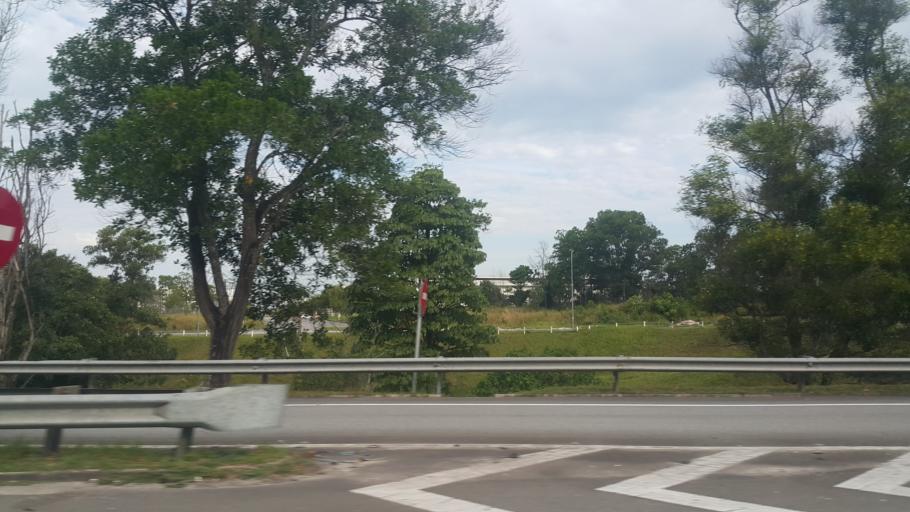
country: MY
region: Johor
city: Skudai
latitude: 1.4359
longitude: 103.6078
